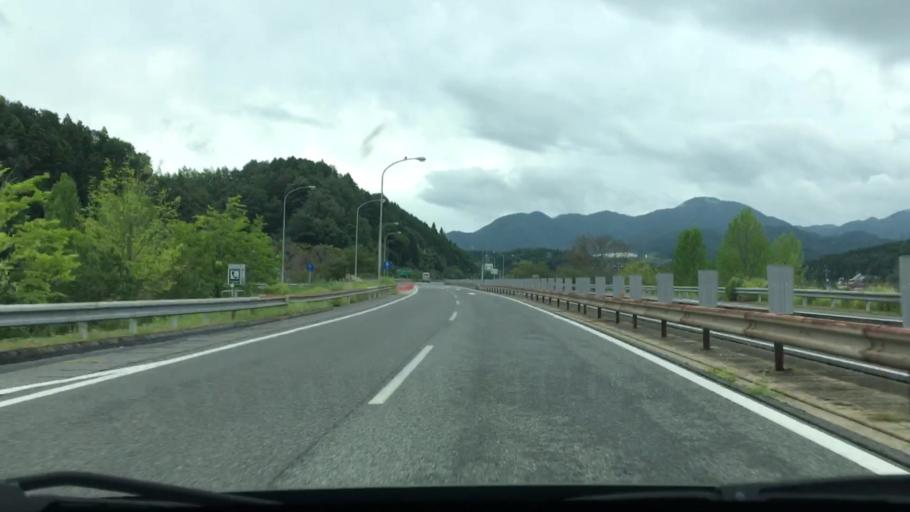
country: JP
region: Hiroshima
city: Hiroshima-shi
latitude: 34.6725
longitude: 132.5435
